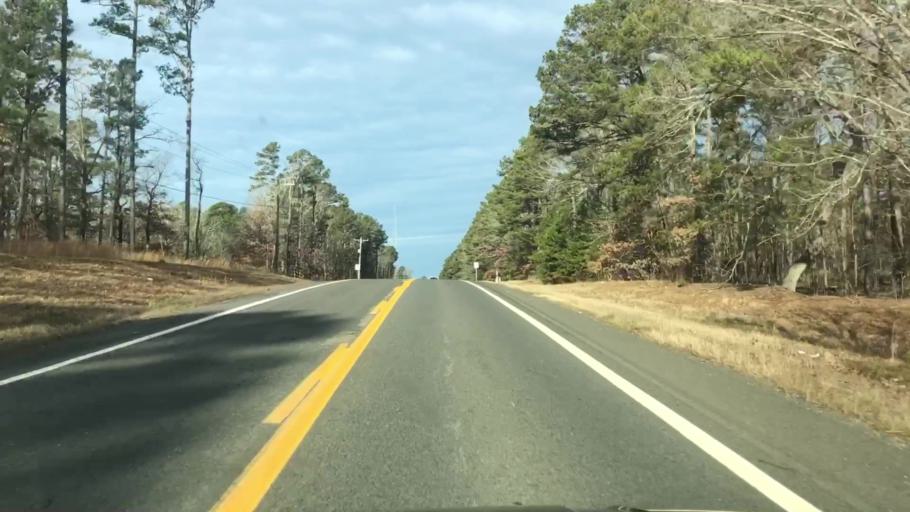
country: US
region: Arkansas
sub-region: Montgomery County
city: Mount Ida
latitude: 34.5422
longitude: -93.6106
